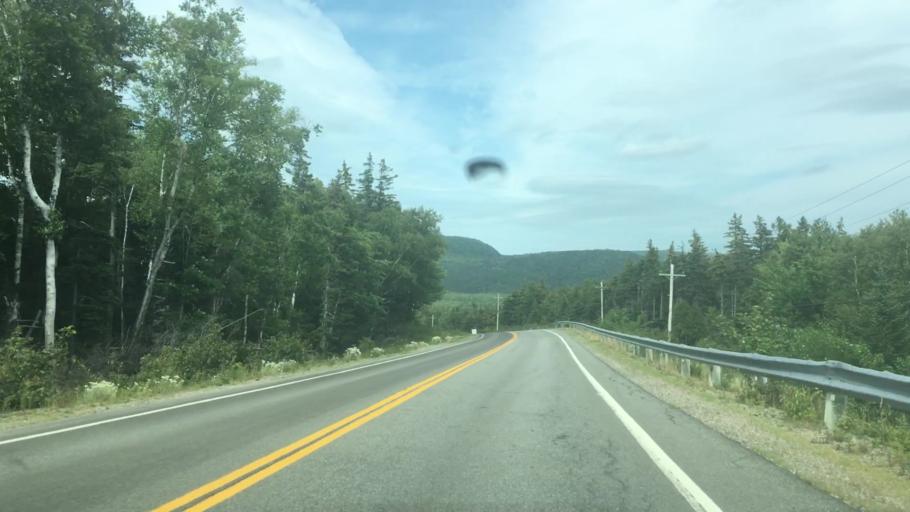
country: CA
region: Nova Scotia
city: Sydney Mines
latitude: 46.5399
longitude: -60.4141
